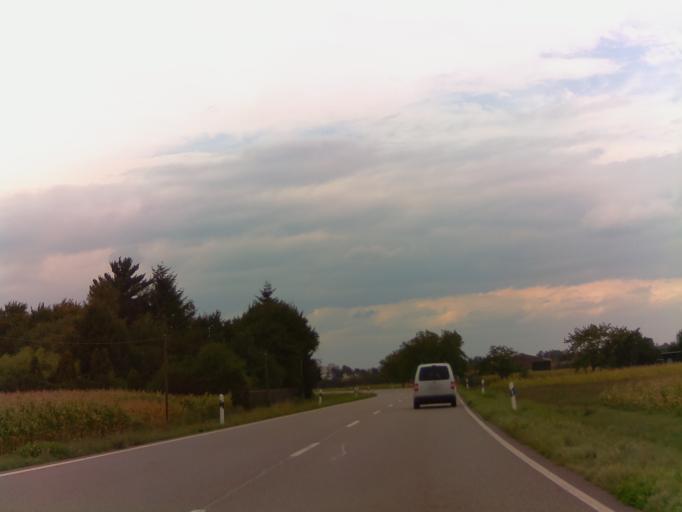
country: DE
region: Hesse
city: Viernheim
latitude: 49.5366
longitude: 8.6090
